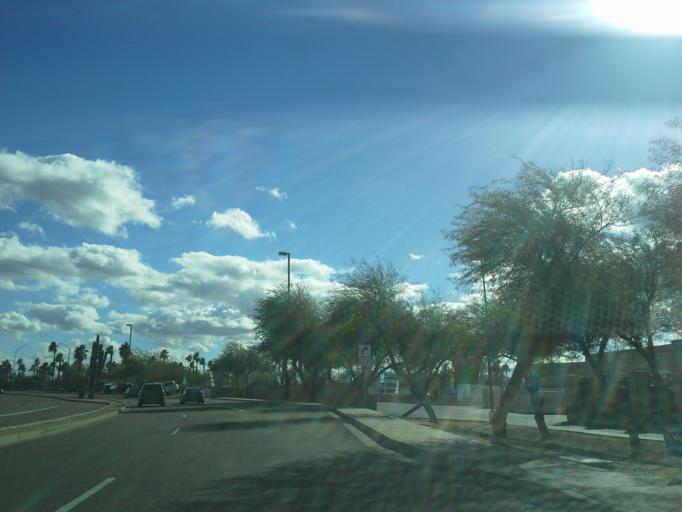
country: US
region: Arizona
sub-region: Maricopa County
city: Gilbert
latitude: 33.3921
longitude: -111.6978
